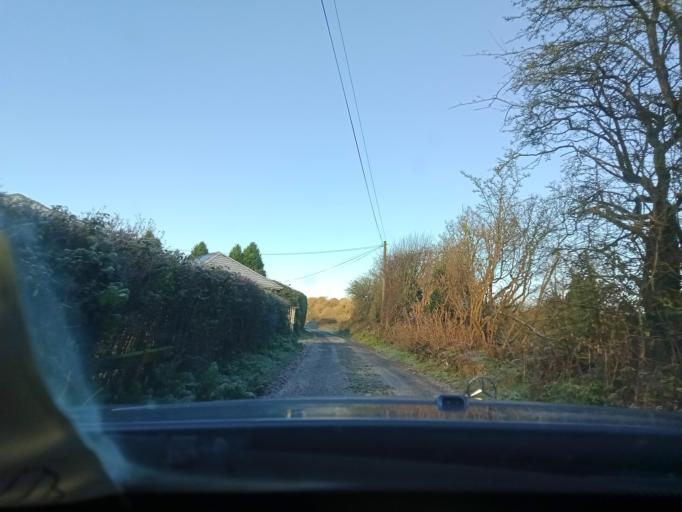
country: IE
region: Leinster
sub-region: Kilkenny
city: Graiguenamanagh
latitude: 52.5989
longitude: -6.9523
